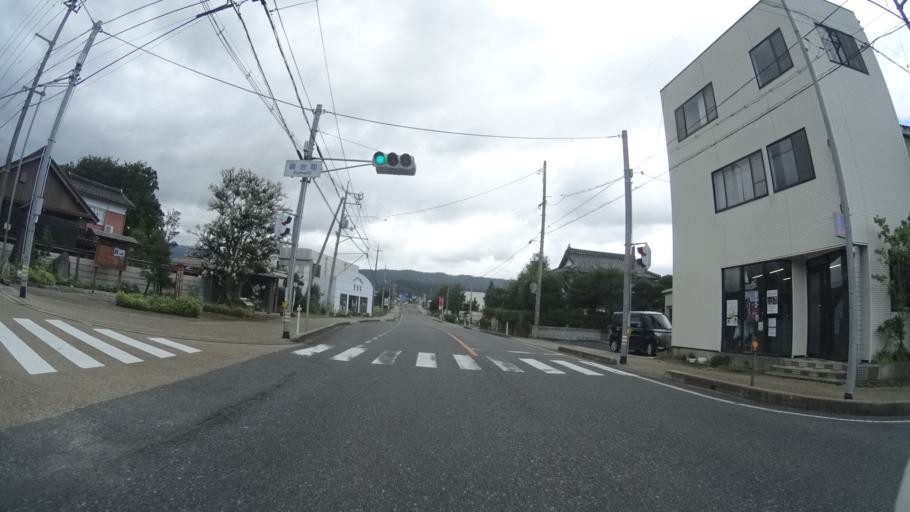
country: JP
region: Tottori
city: Tottori
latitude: 35.4640
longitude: 134.0626
